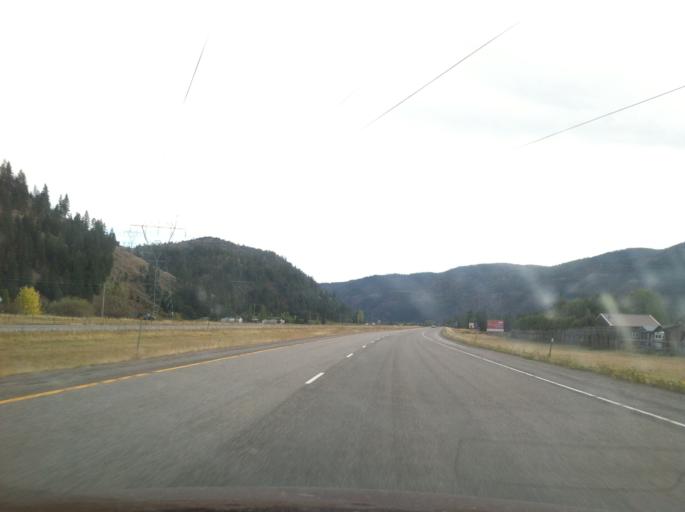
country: US
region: Montana
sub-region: Missoula County
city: Clinton
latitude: 46.7763
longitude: -113.7116
